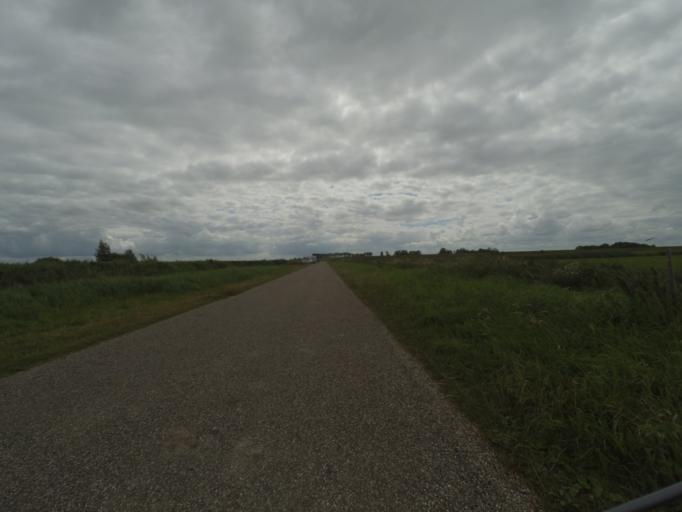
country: NL
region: Friesland
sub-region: Gemeente Dongeradeel
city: Anjum
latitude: 53.3441
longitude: 6.1529
